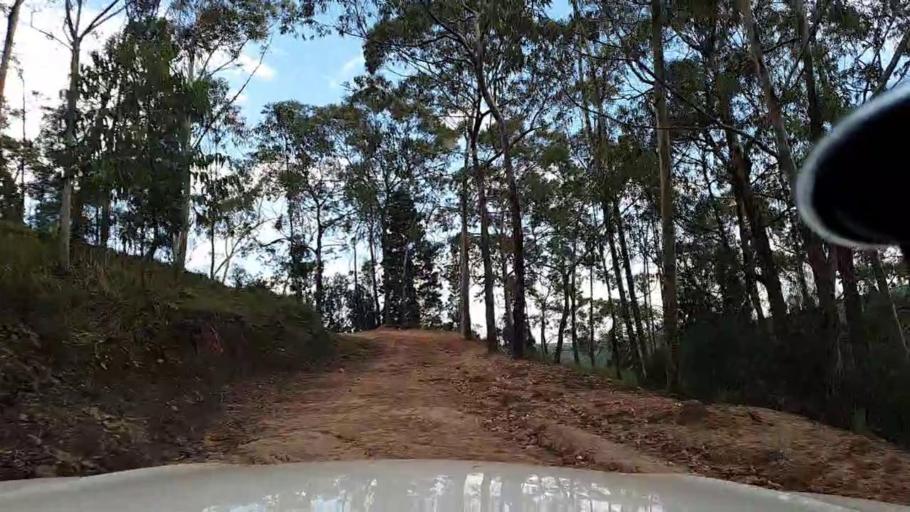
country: RW
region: Southern Province
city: Gitarama
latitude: -1.8090
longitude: 29.8027
